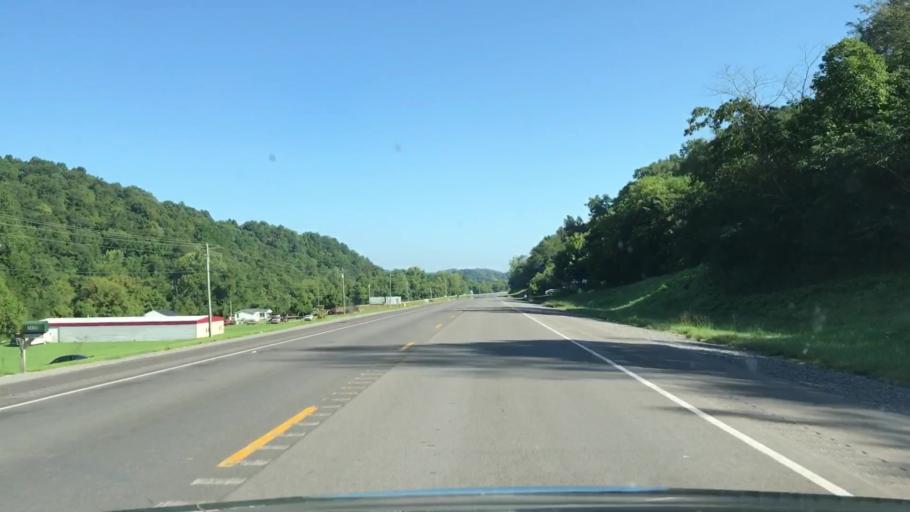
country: US
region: Kentucky
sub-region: Cumberland County
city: Burkesville
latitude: 36.7351
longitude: -85.3731
